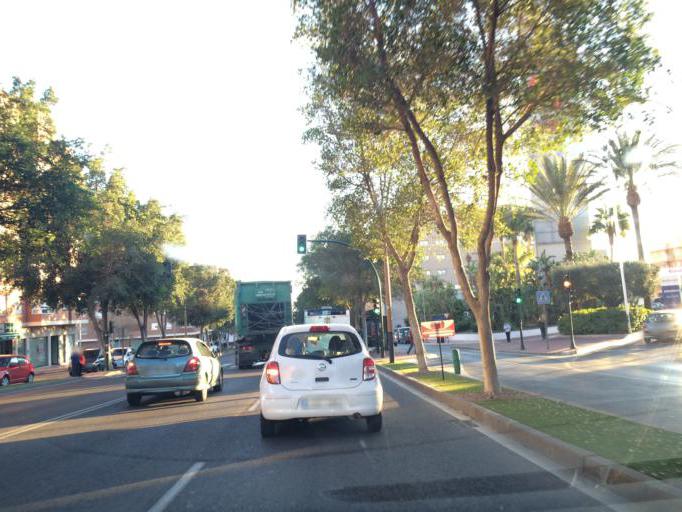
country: ES
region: Andalusia
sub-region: Provincia de Almeria
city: Almeria
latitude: 36.8532
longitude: -2.4463
